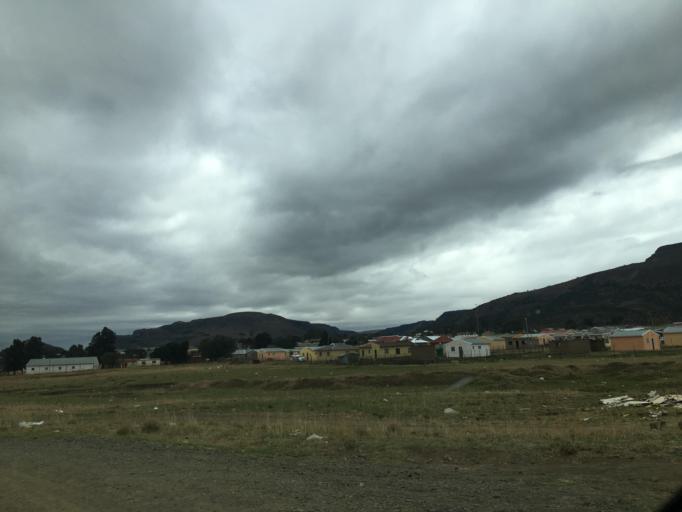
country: ZA
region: Eastern Cape
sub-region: Chris Hani District Municipality
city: Cala
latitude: -31.5344
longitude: 27.6951
